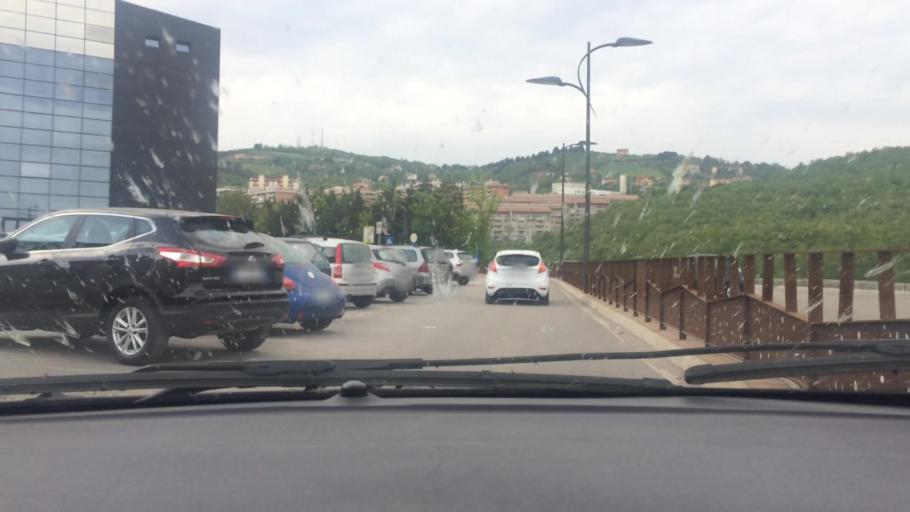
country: IT
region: Basilicate
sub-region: Provincia di Potenza
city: Potenza
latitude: 40.6525
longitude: 15.8073
